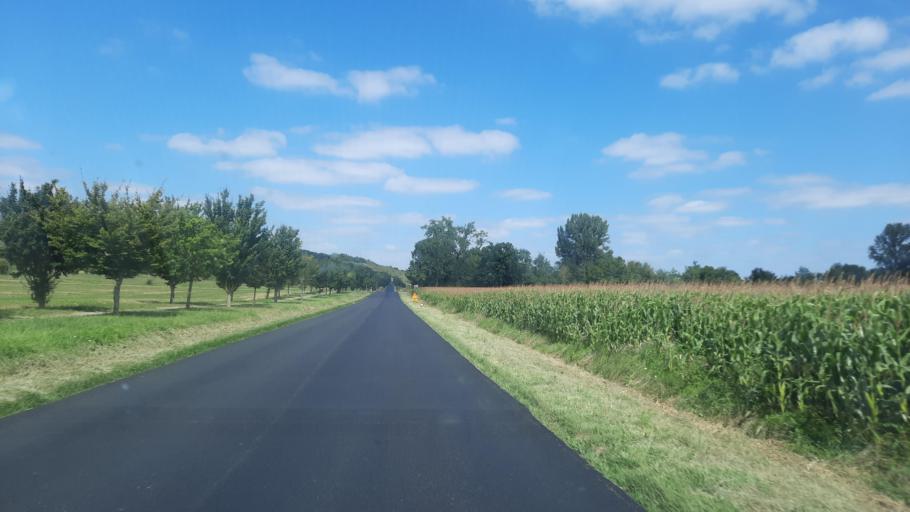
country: FR
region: Midi-Pyrenees
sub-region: Departement du Gers
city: Lombez
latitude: 43.4628
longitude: 0.8882
